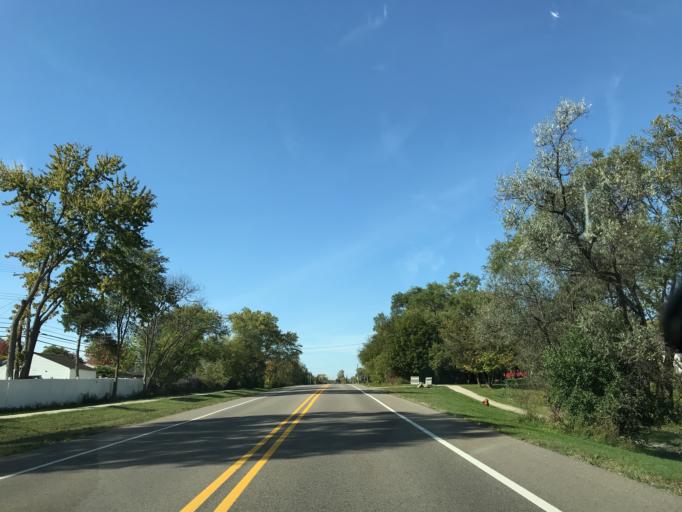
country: US
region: Michigan
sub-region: Oakland County
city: Farmington
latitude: 42.4701
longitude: -83.3632
